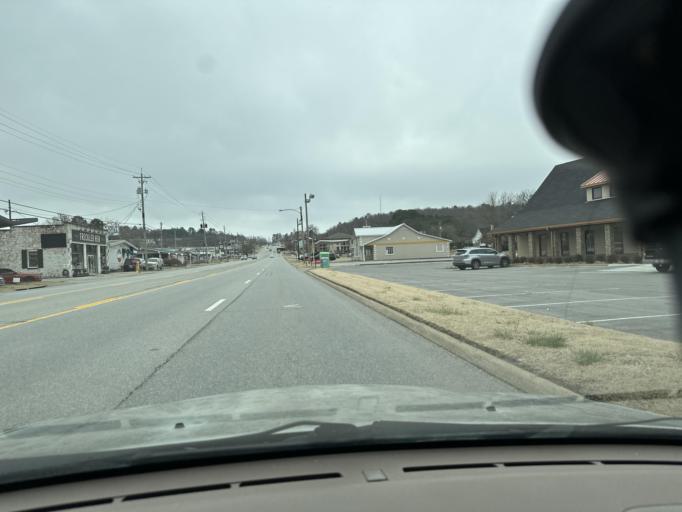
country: US
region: Arkansas
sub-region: Washington County
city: Fayetteville
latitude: 36.0879
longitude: -94.1547
